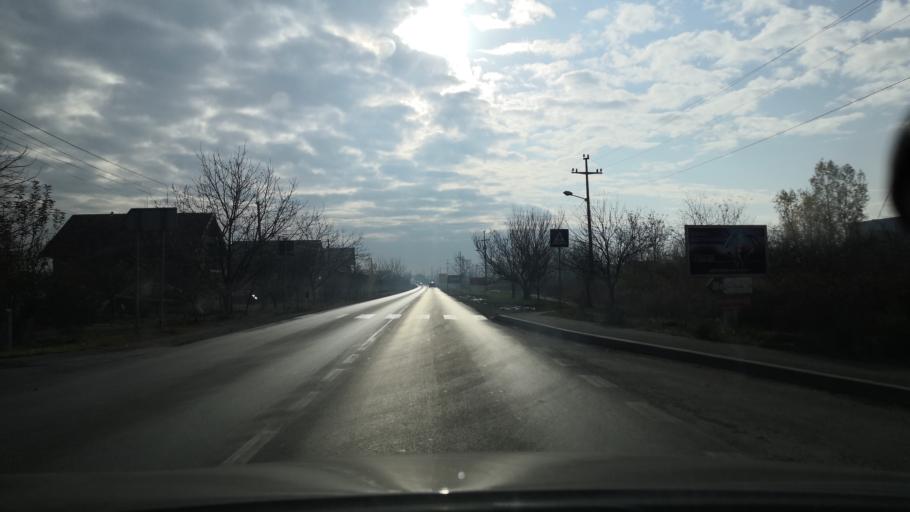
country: RS
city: Ugrinovci
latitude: 44.8525
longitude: 20.2062
